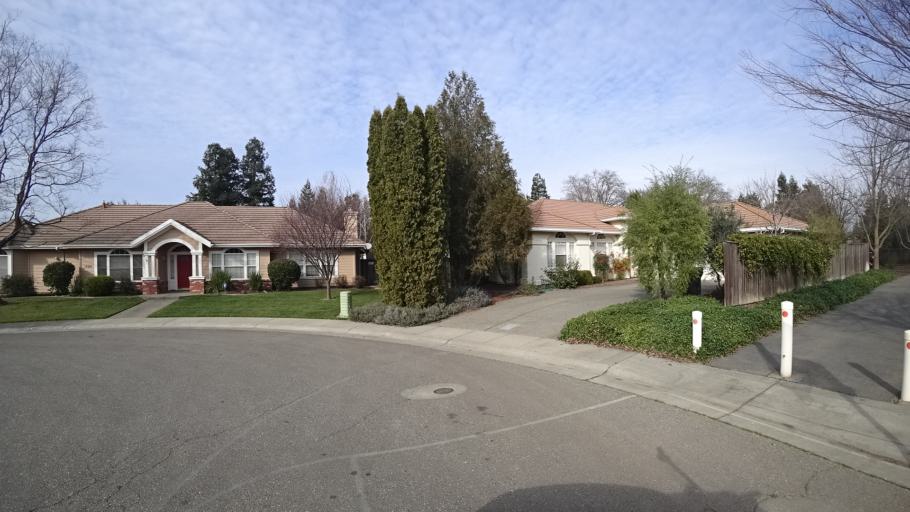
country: US
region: California
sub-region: Yolo County
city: Davis
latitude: 38.5360
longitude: -121.7202
